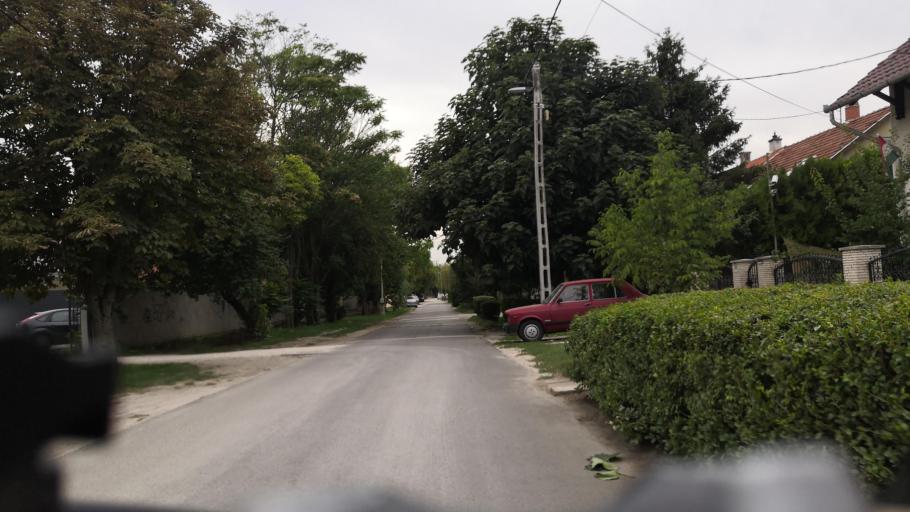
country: HU
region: Csongrad
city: Szeged
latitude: 46.2739
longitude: 20.1581
